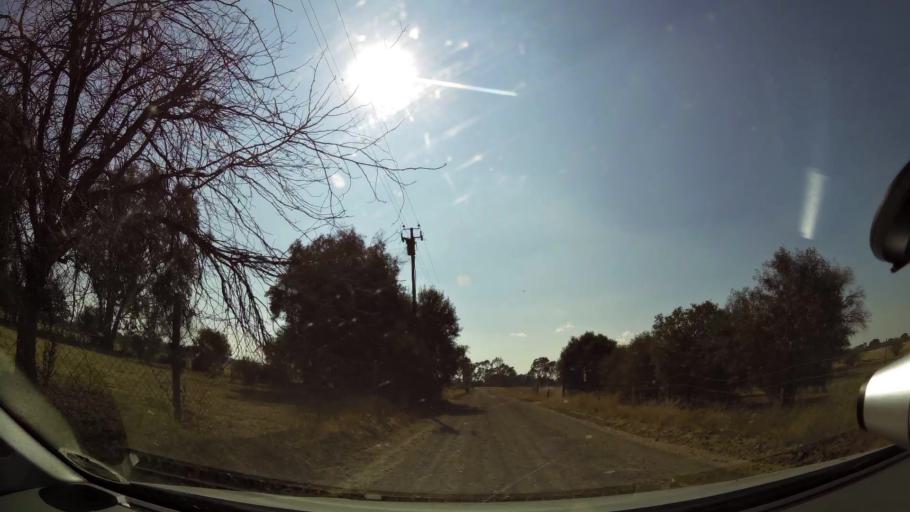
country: ZA
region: Orange Free State
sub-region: Mangaung Metropolitan Municipality
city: Bloemfontein
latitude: -29.1608
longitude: 26.3120
